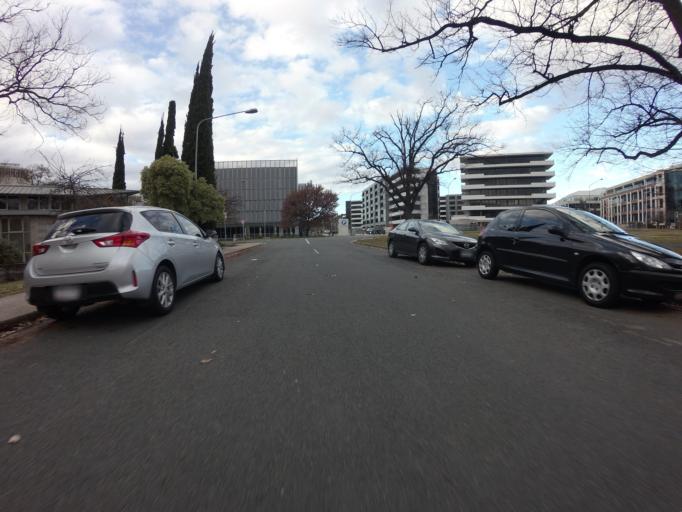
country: AU
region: Australian Capital Territory
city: Forrest
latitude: -35.3066
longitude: 149.1348
